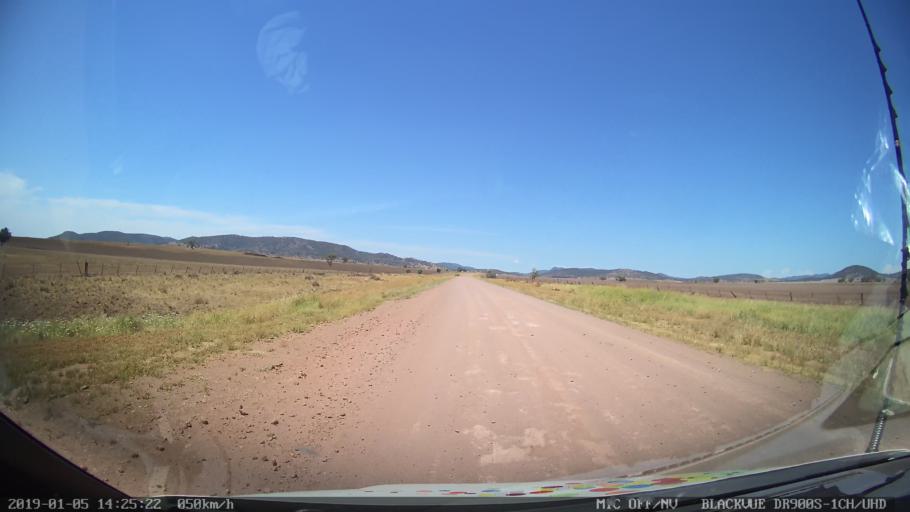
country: AU
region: New South Wales
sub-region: Liverpool Plains
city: Quirindi
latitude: -31.2412
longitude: 150.5490
